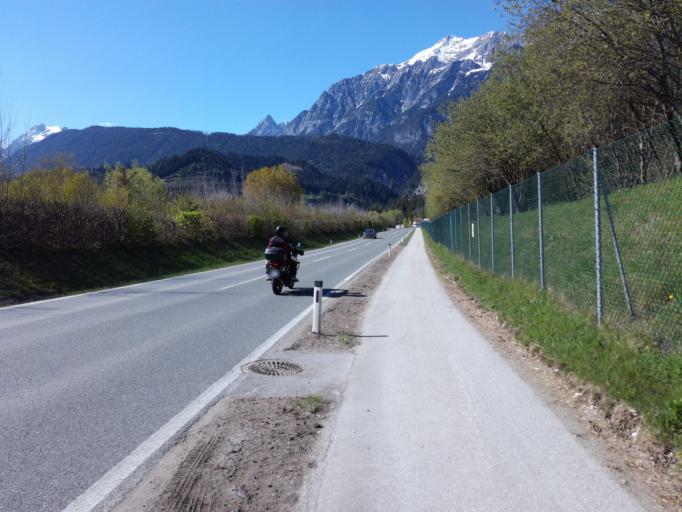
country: AT
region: Tyrol
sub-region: Politischer Bezirk Schwaz
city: Vomp
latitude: 47.3290
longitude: 11.6714
